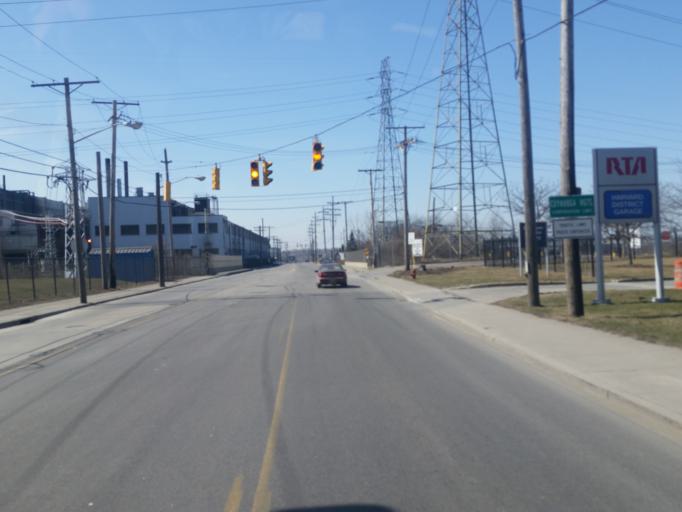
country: US
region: Ohio
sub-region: Cuyahoga County
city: Newburgh Heights
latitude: 41.4477
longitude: -81.6720
